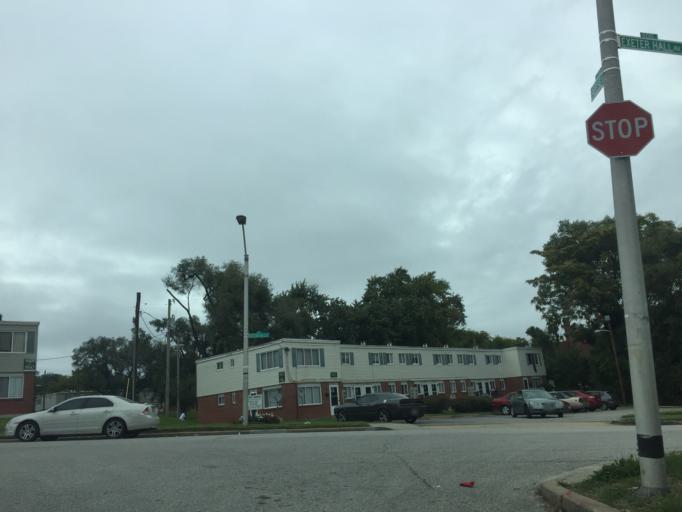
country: US
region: Maryland
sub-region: City of Baltimore
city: Baltimore
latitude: 39.3221
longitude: -76.6057
